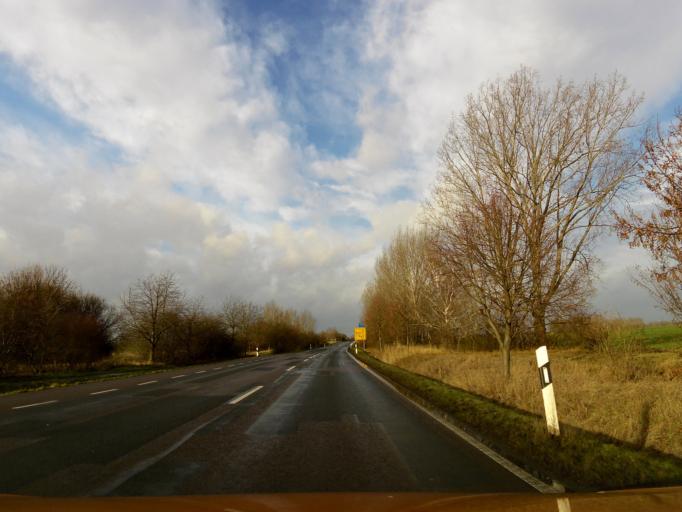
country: DE
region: Saxony-Anhalt
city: Ebendorf
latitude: 52.1880
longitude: 11.5683
